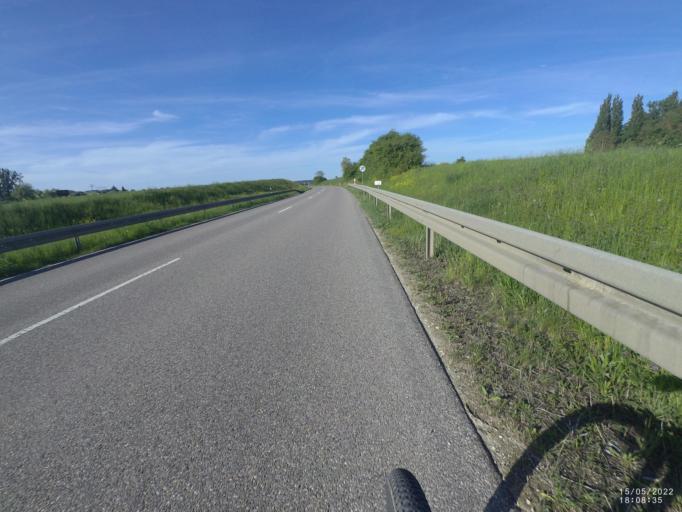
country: DE
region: Baden-Wuerttemberg
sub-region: Regierungsbezirk Stuttgart
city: Bolheim
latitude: 48.5939
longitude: 10.1354
